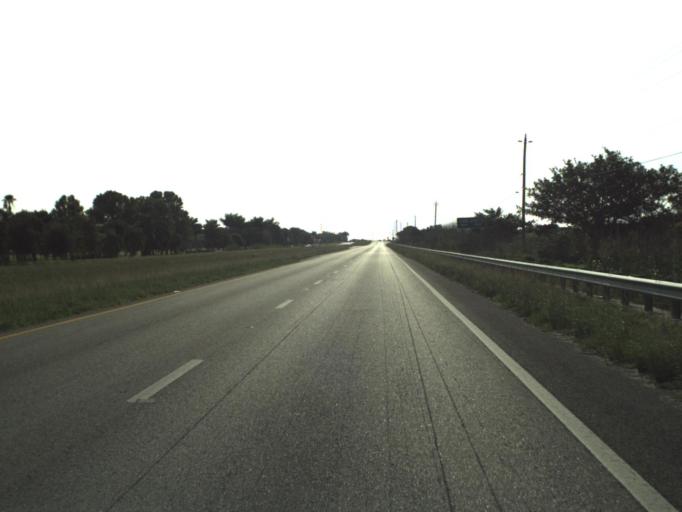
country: US
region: Florida
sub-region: Palm Beach County
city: South Bay
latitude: 26.6959
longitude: -80.8141
